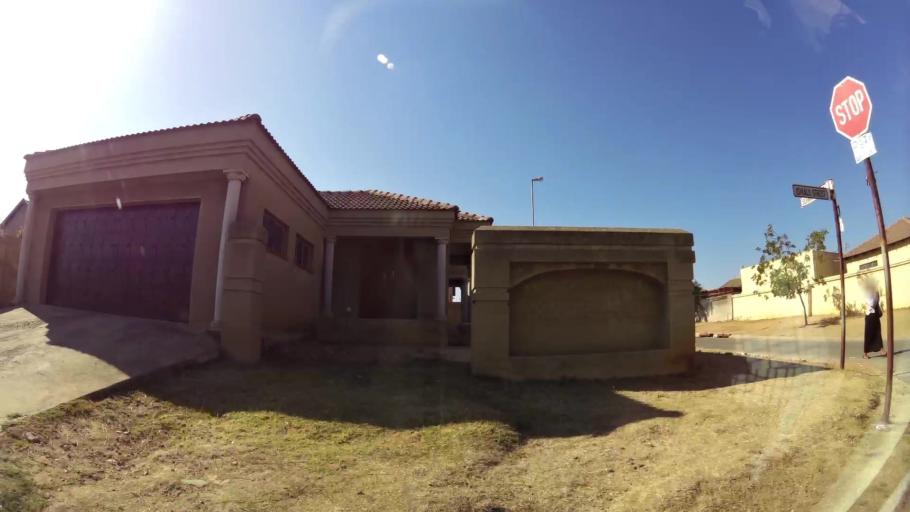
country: ZA
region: Gauteng
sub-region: Ekurhuleni Metropolitan Municipality
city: Tembisa
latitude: -26.0416
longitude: 28.1972
